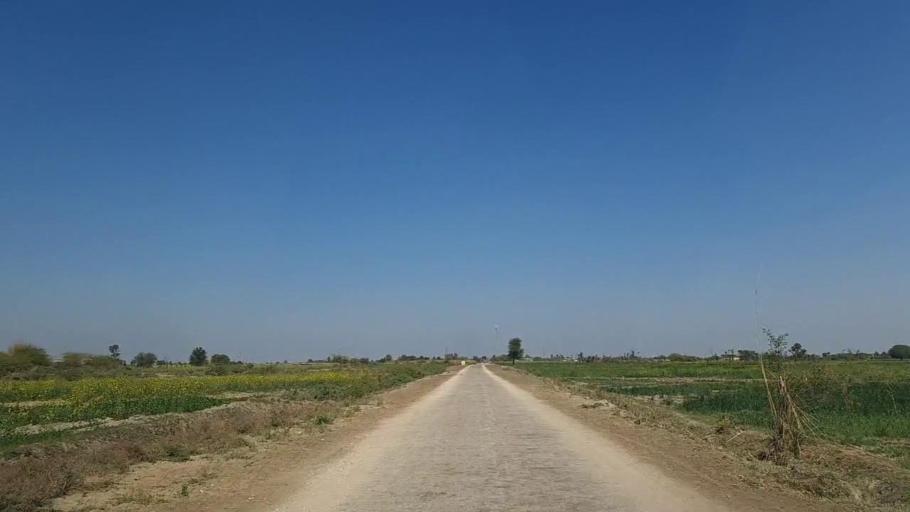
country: PK
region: Sindh
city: Samaro
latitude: 25.0960
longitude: 69.3995
